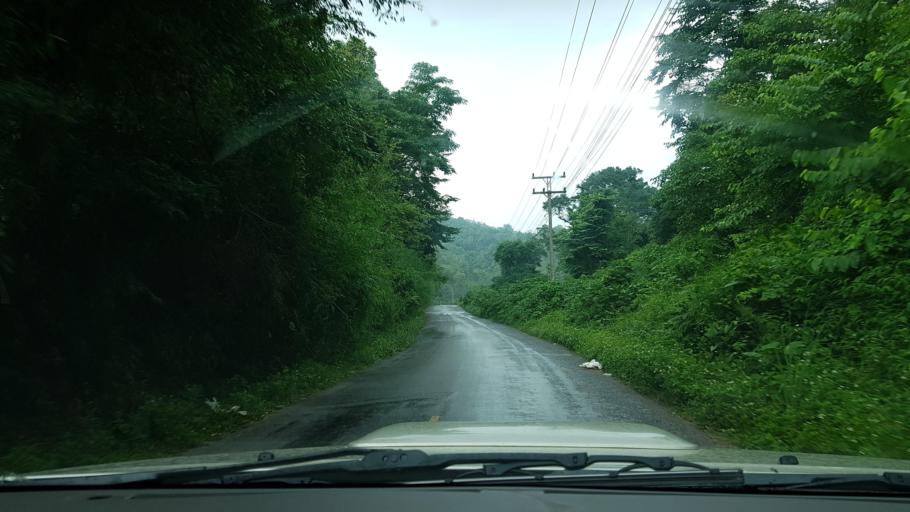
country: LA
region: Oudomxai
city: Muang Xay
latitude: 20.6133
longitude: 101.9510
